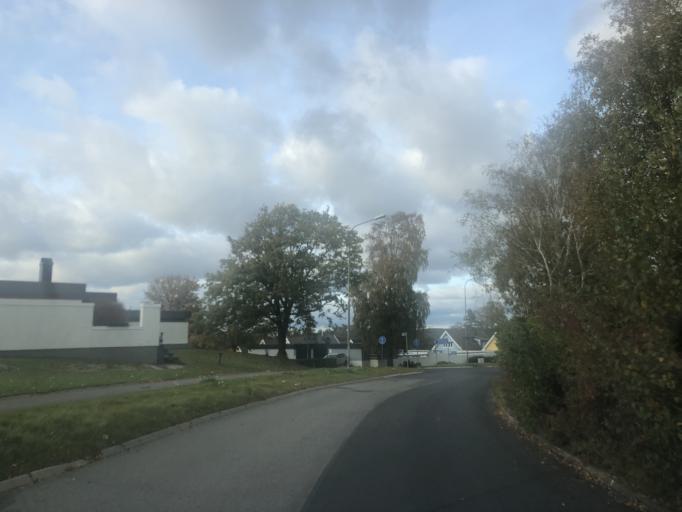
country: SE
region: Vaestra Goetaland
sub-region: Goteborg
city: Majorna
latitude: 57.6329
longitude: 11.9485
